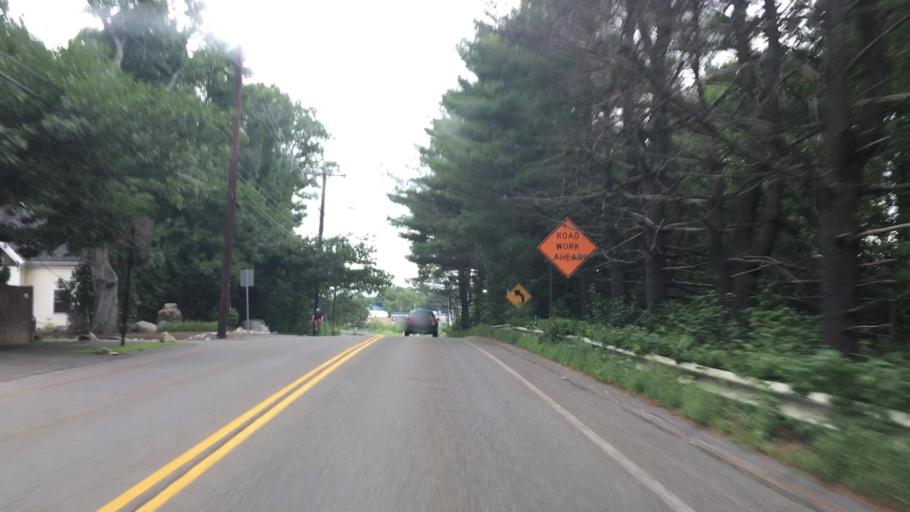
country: US
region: Massachusetts
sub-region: Middlesex County
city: Lexington
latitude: 42.4692
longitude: -71.2094
